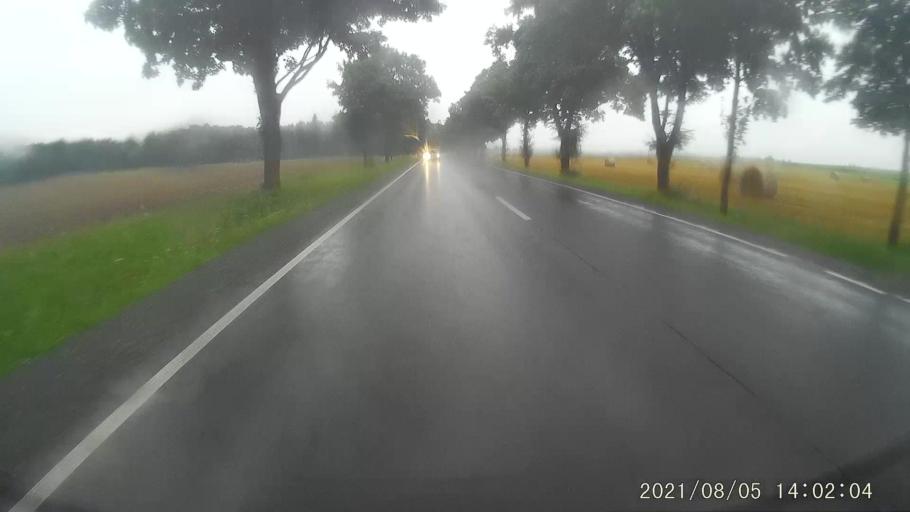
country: PL
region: Opole Voivodeship
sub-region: Powiat krapkowicki
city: Strzeleczki
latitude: 50.4528
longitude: 17.8817
